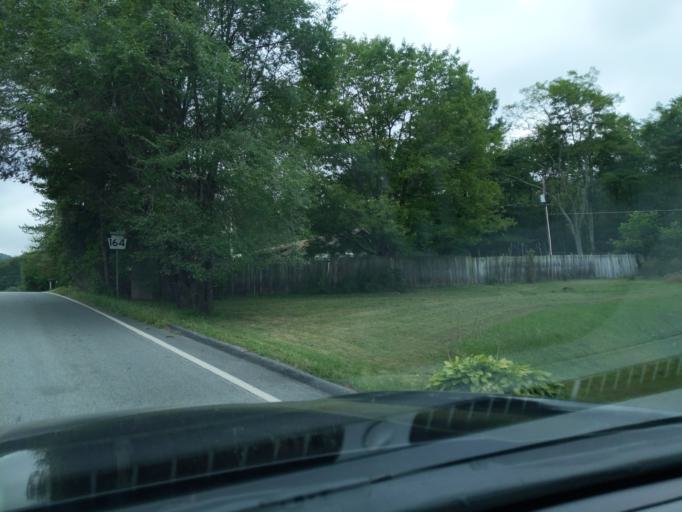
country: US
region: Pennsylvania
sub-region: Blair County
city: Claysburg
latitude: 40.3579
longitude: -78.4866
